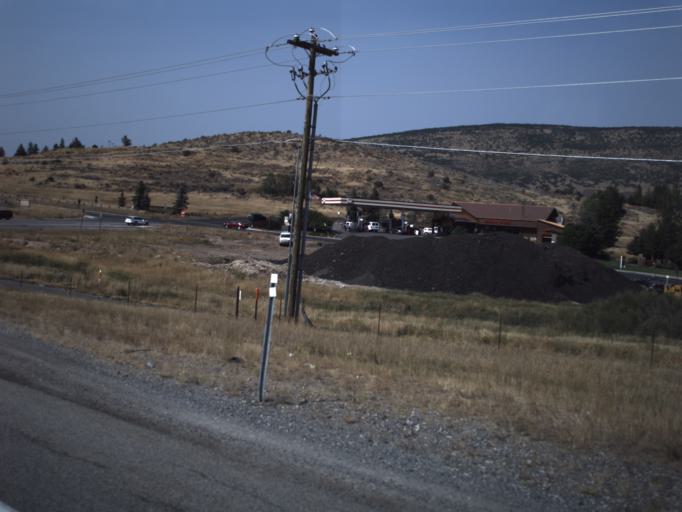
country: US
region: Utah
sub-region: Summit County
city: Summit Park
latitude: 40.7538
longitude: -111.5709
